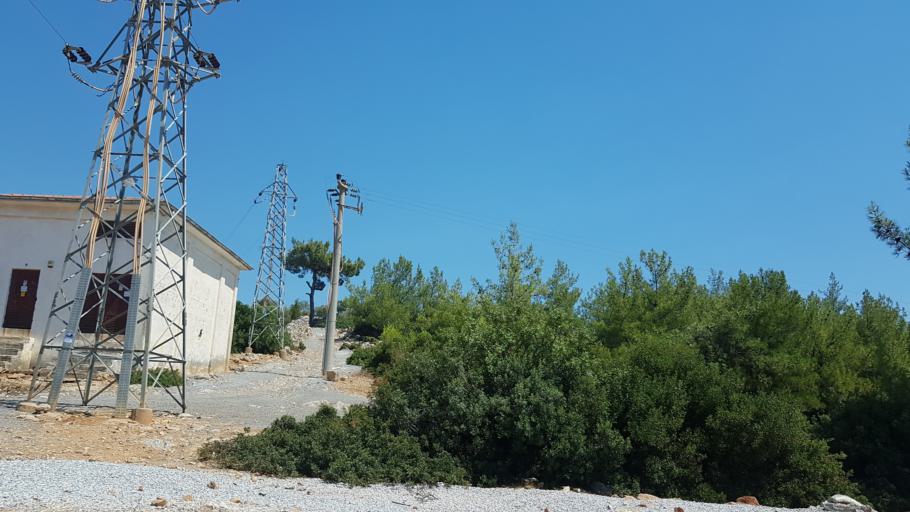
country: TR
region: Mugla
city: Karaova
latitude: 37.0273
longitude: 27.7384
